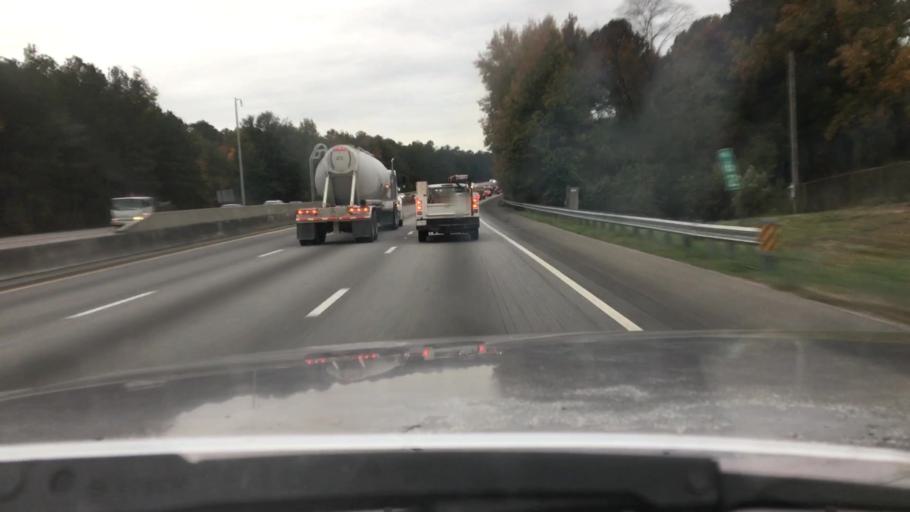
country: US
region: South Carolina
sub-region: Lexington County
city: Saint Andrews
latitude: 34.0162
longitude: -81.1397
